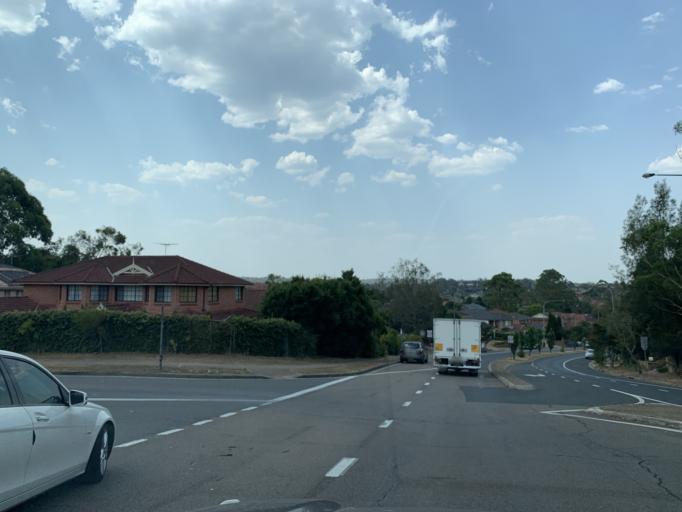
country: AU
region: New South Wales
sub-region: The Hills Shire
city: West Pennant
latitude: -33.7313
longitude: 151.0286
